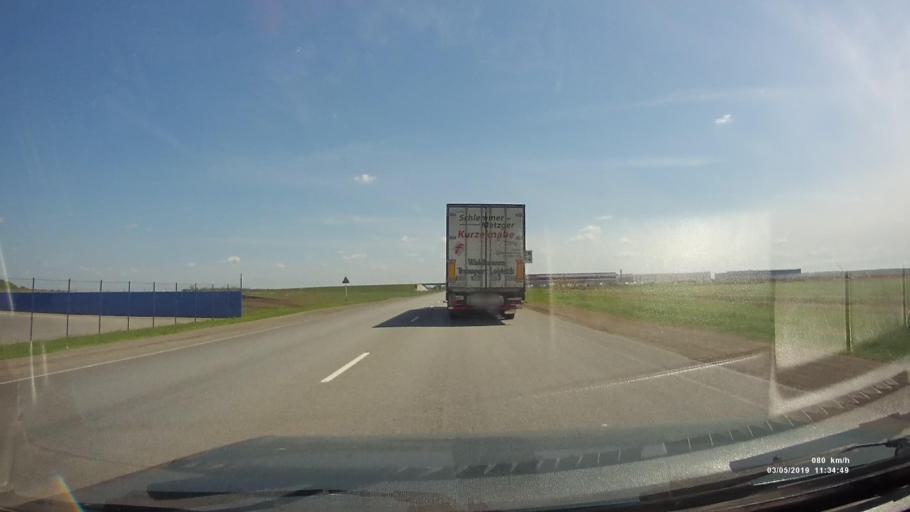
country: RU
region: Rostov
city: Ol'ginskaya
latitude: 47.1294
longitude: 39.8915
